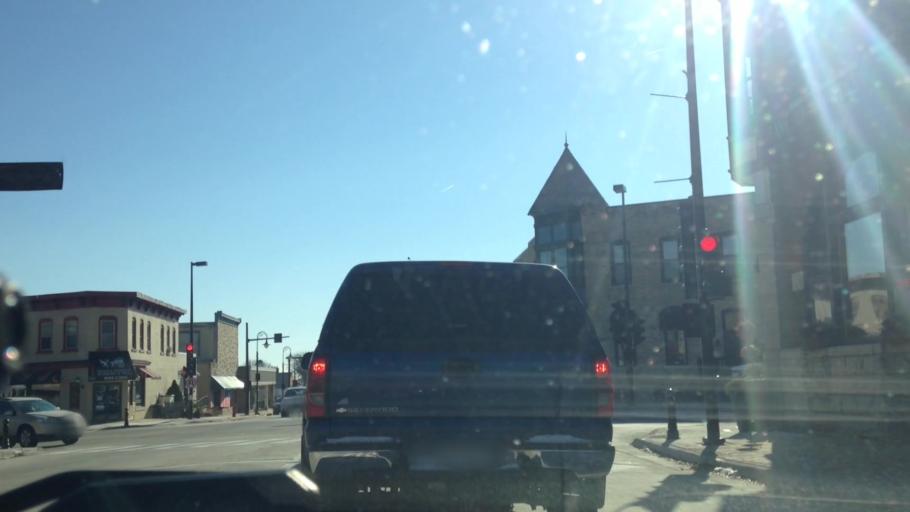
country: US
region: Wisconsin
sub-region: Waukesha County
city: Menomonee Falls
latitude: 43.1791
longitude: -88.1175
